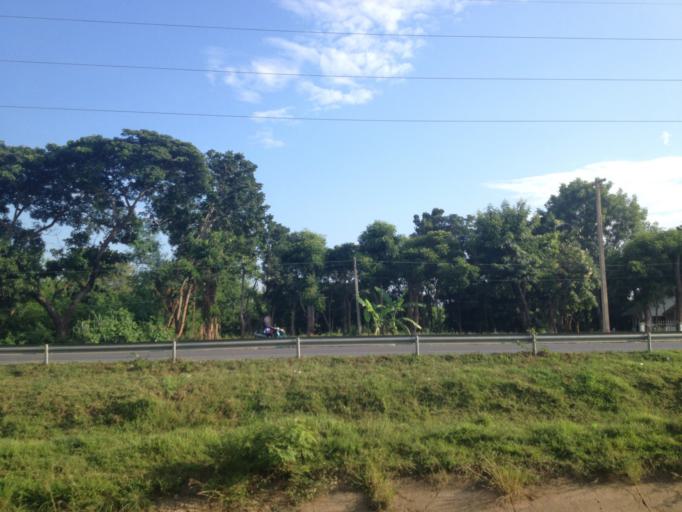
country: TH
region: Chiang Mai
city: Hang Dong
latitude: 18.7066
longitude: 98.9098
